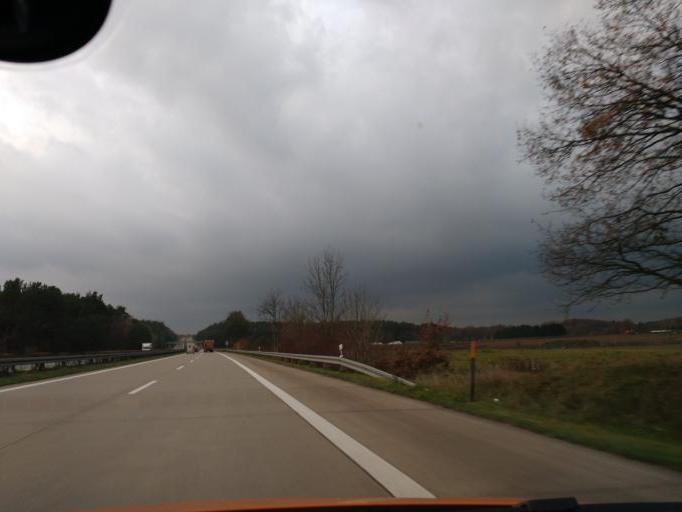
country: DE
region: Brandenburg
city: Heiligengrabe
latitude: 53.1697
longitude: 12.3566
